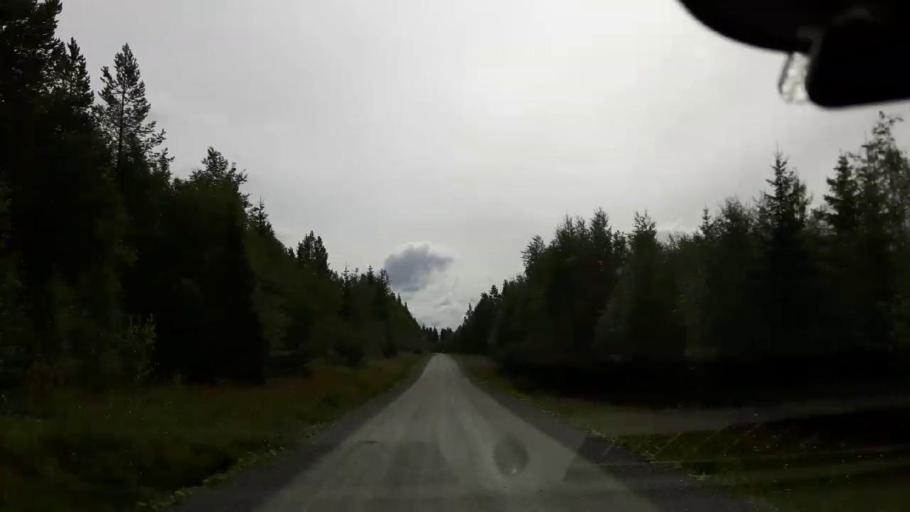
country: SE
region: Jaemtland
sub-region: Krokoms Kommun
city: Valla
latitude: 63.6336
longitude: 14.0181
